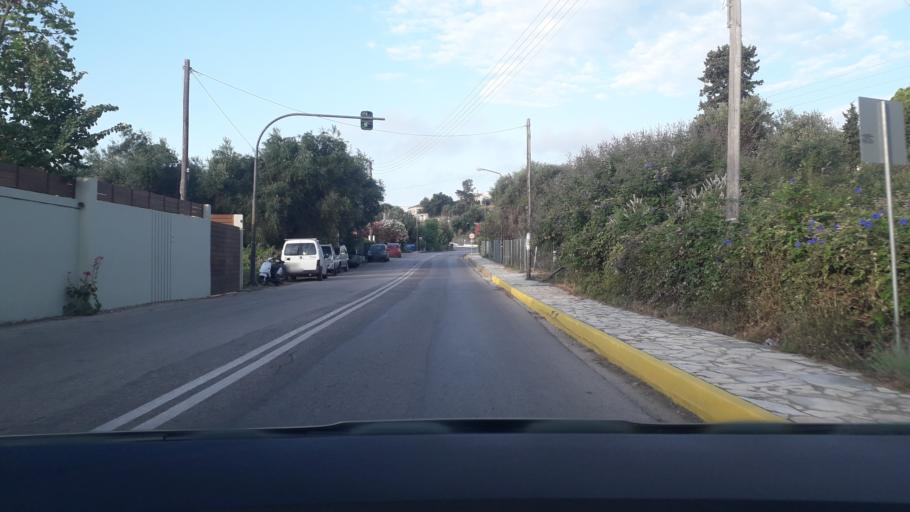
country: GR
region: Ionian Islands
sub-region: Nomos Kerkyras
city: Agios Matthaios
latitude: 39.4891
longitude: 19.9266
